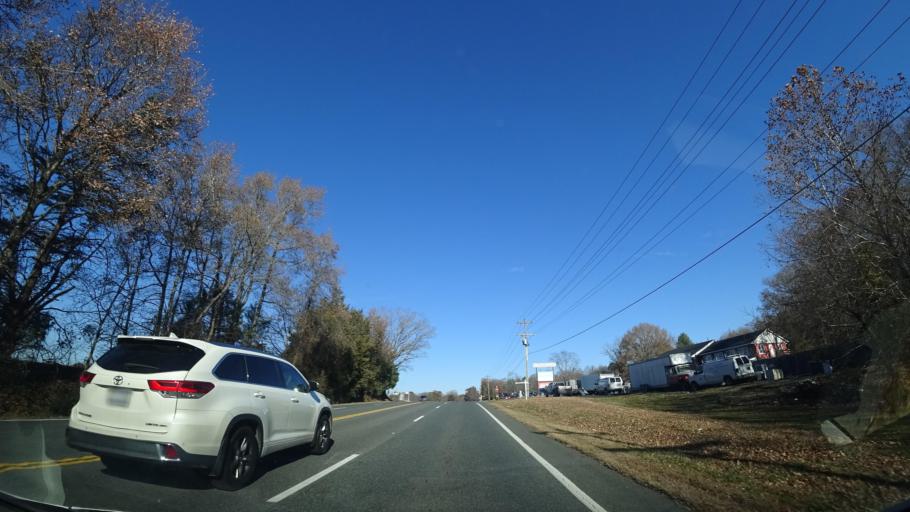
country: US
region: Virginia
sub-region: Spotsylvania County
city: Spotsylvania Courthouse
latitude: 38.1431
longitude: -77.5235
